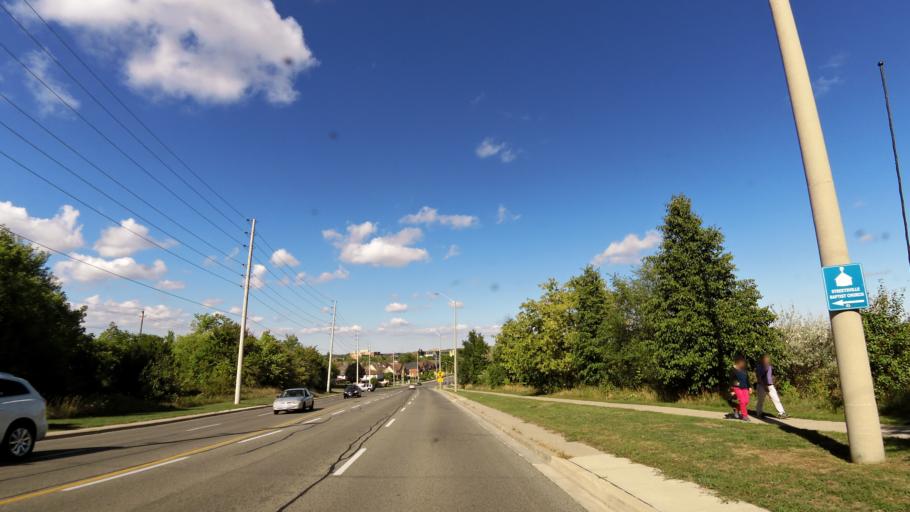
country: CA
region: Ontario
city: Mississauga
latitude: 43.5733
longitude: -79.7185
